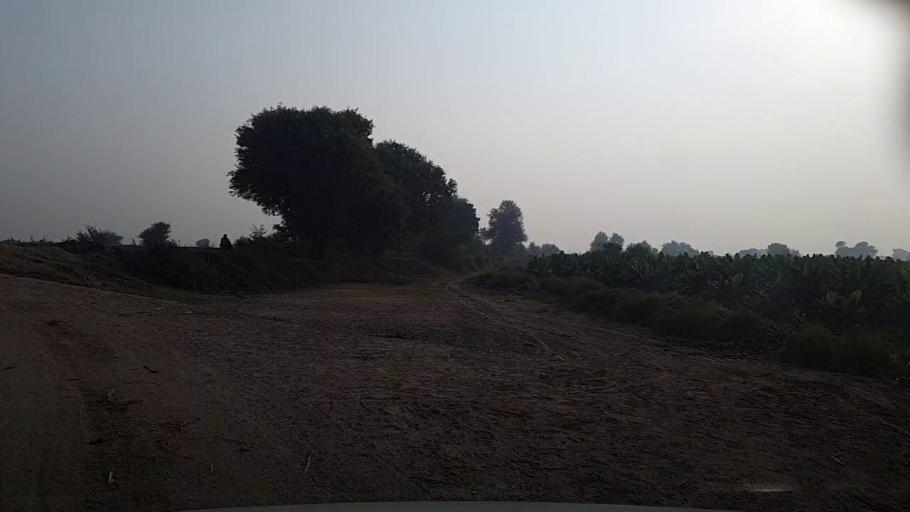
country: PK
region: Sindh
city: Kandiari
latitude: 27.0054
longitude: 68.4941
